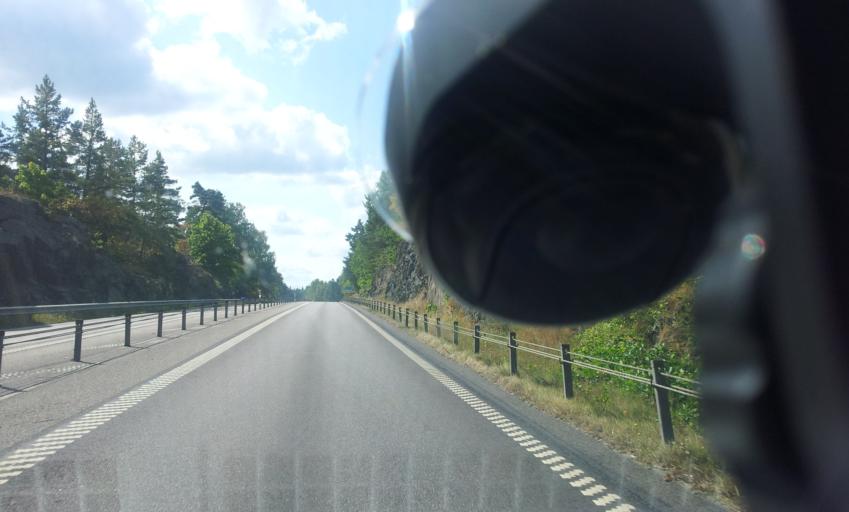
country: SE
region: Kalmar
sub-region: Oskarshamns Kommun
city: Oskarshamn
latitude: 57.3371
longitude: 16.4833
